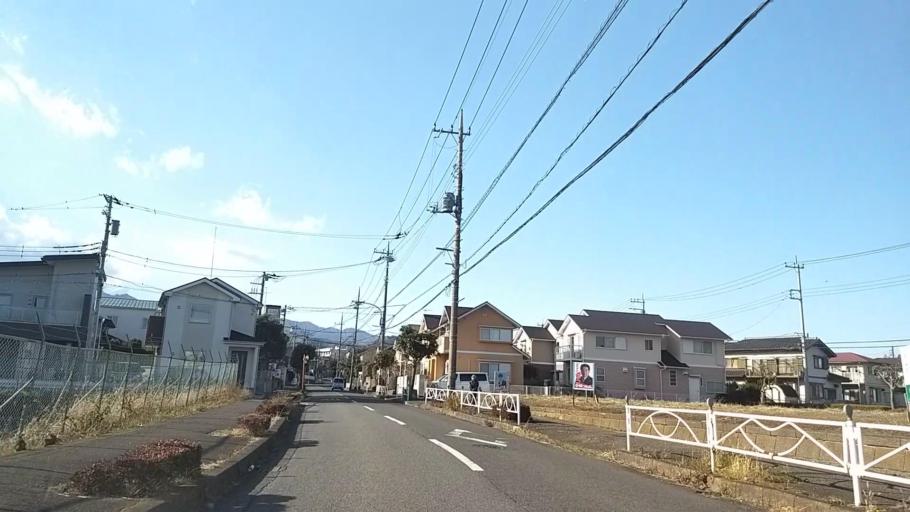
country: JP
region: Kanagawa
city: Atsugi
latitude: 35.4620
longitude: 139.3284
